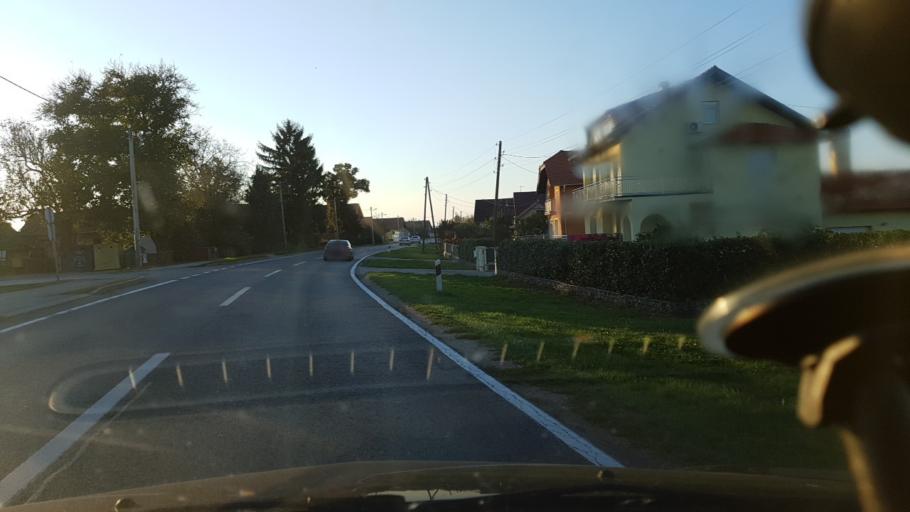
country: HR
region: Koprivnicko-Krizevacka
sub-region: Grad Koprivnica
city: Koprivnica
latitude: 46.1343
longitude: 16.8616
